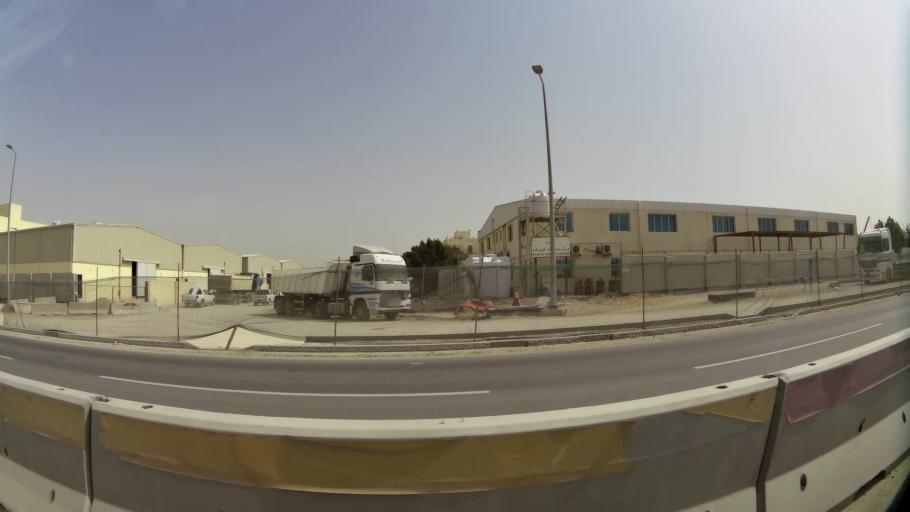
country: QA
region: Baladiyat ar Rayyan
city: Ar Rayyan
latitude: 25.1895
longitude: 51.4206
